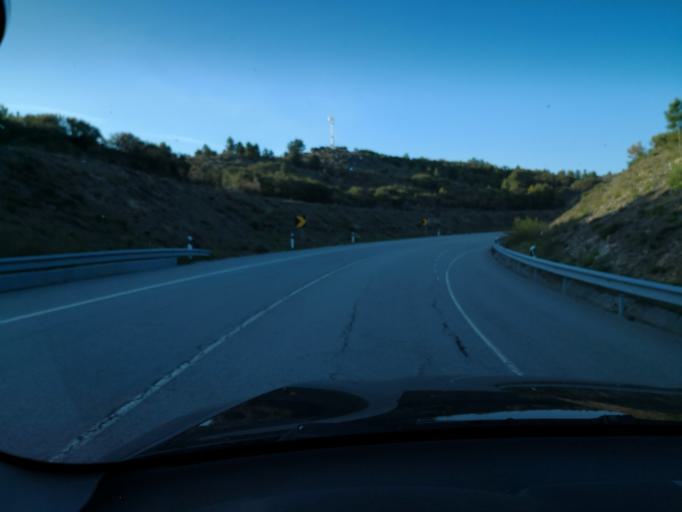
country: PT
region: Vila Real
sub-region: Vila Real
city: Vila Real
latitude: 41.3685
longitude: -7.7130
